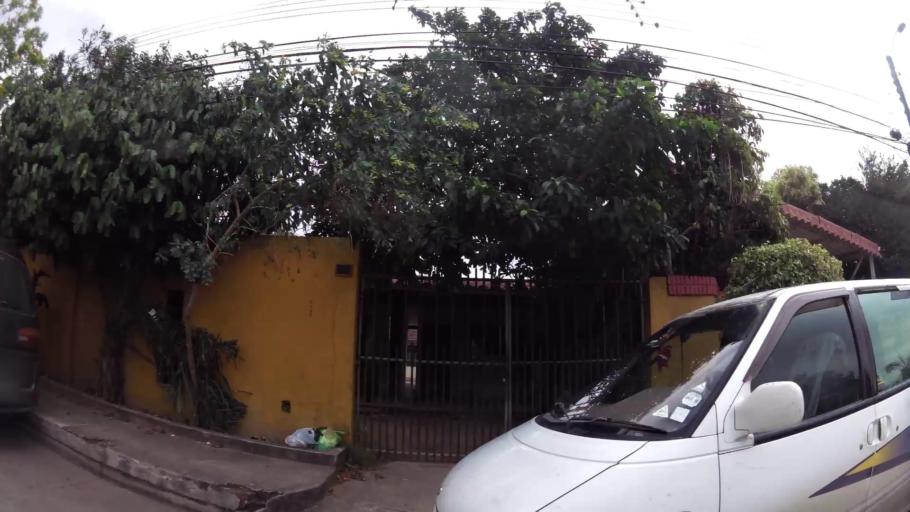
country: BO
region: Santa Cruz
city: Santa Cruz de la Sierra
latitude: -17.7699
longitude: -63.2039
